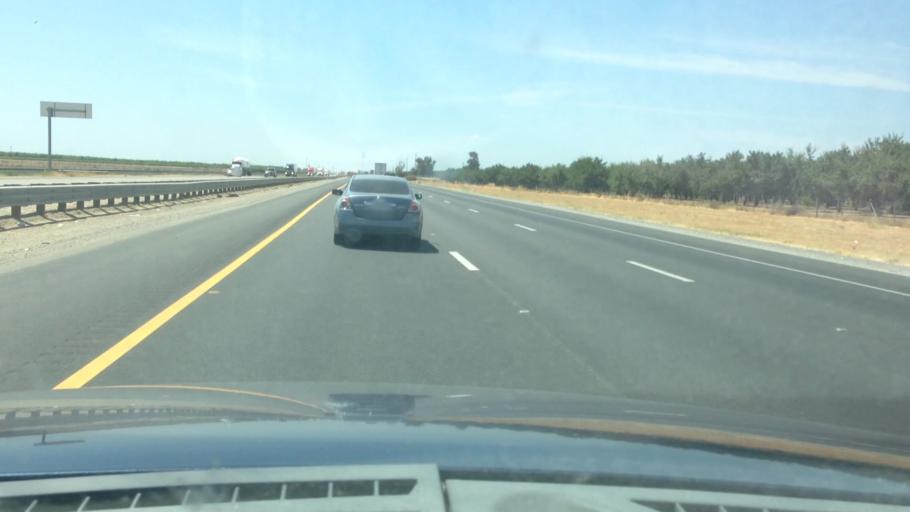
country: US
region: California
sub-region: Kern County
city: McFarland
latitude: 35.6364
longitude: -119.2174
